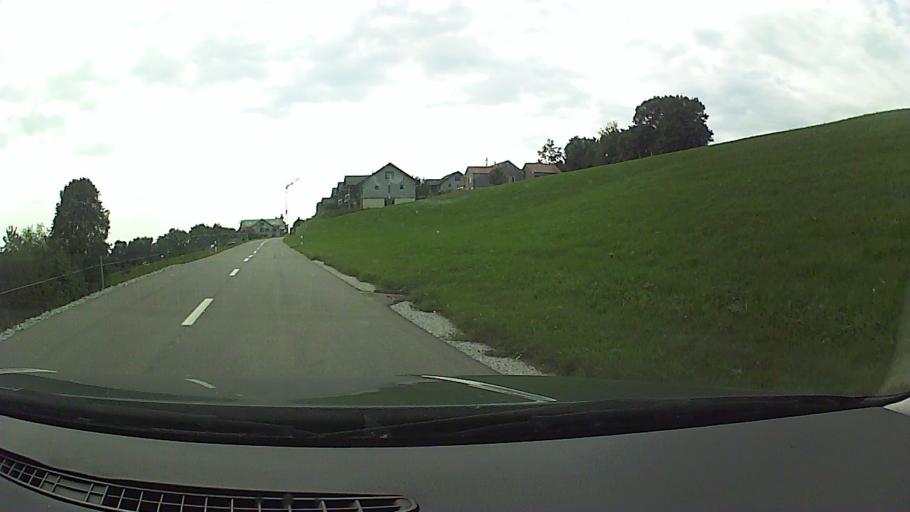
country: CH
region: Fribourg
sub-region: Veveyse District
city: Chatel-Saint-Denis
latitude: 46.5872
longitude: 6.8963
